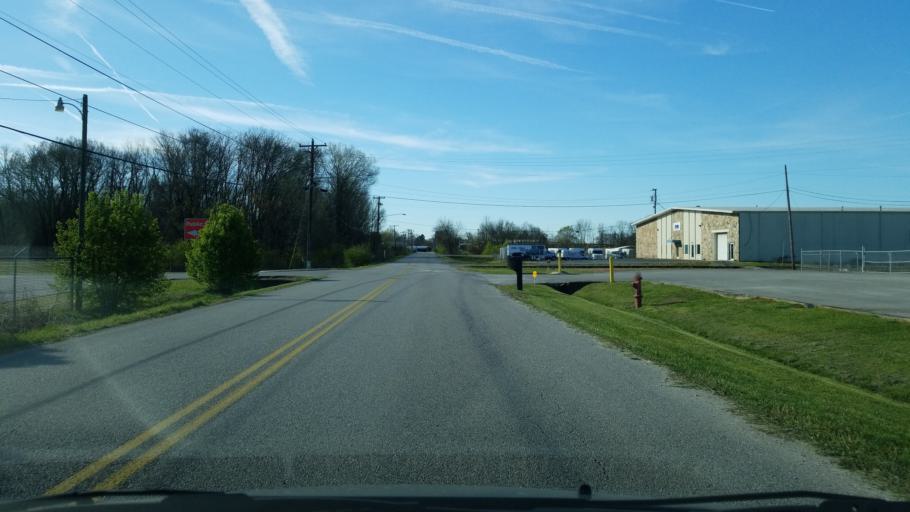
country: US
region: Tennessee
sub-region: Hamilton County
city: East Chattanooga
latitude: 35.0499
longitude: -85.1937
